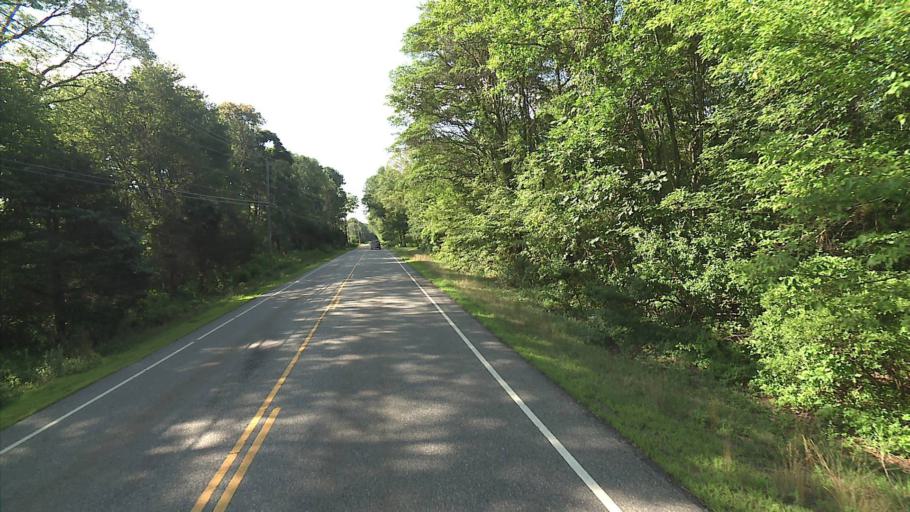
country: US
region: Connecticut
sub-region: New London County
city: Montville Center
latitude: 41.5208
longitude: -72.2051
